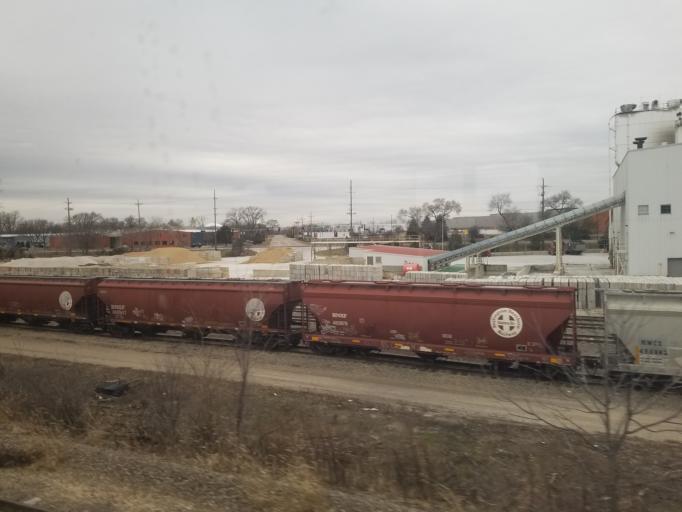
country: US
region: Illinois
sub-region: Kane County
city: Montgomery
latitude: 41.7346
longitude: -88.3403
